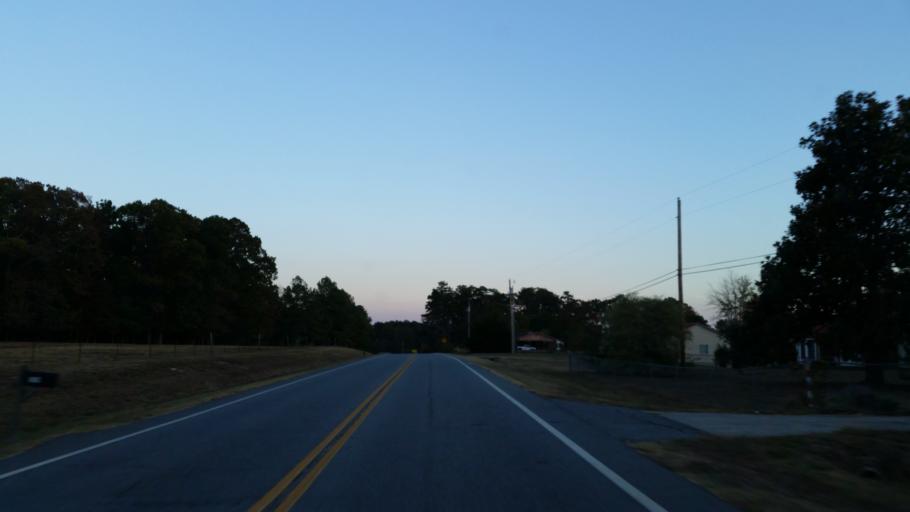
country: US
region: Georgia
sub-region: Gordon County
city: Calhoun
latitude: 34.5909
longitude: -85.0209
